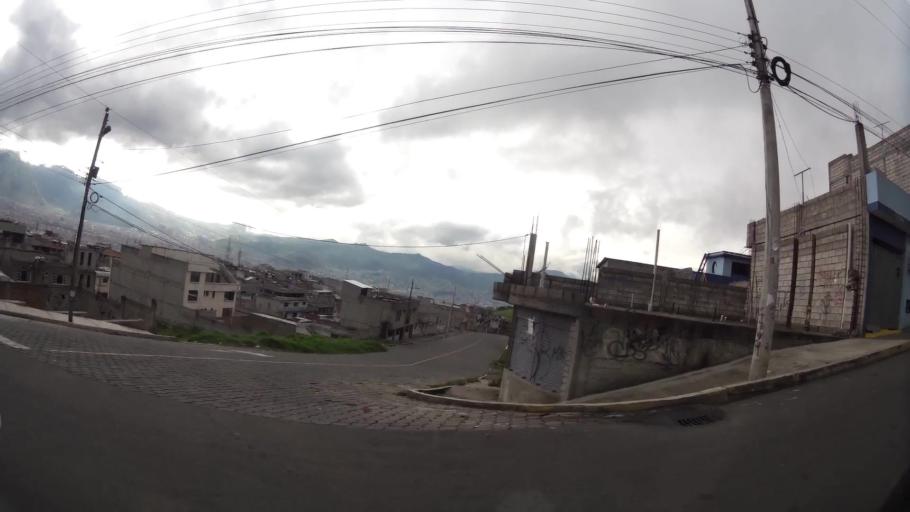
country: EC
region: Pichincha
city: Sangolqui
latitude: -0.3078
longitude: -78.5244
